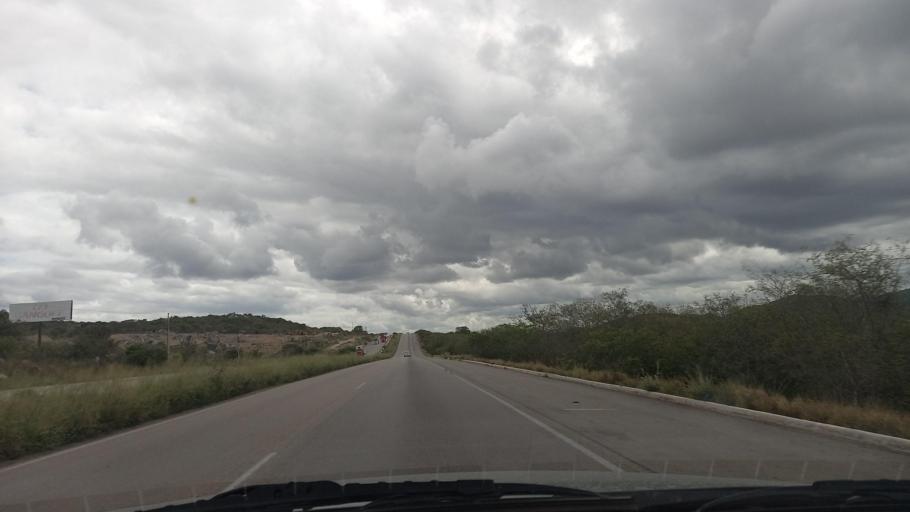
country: BR
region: Pernambuco
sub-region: Caruaru
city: Caruaru
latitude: -8.3231
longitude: -36.1009
